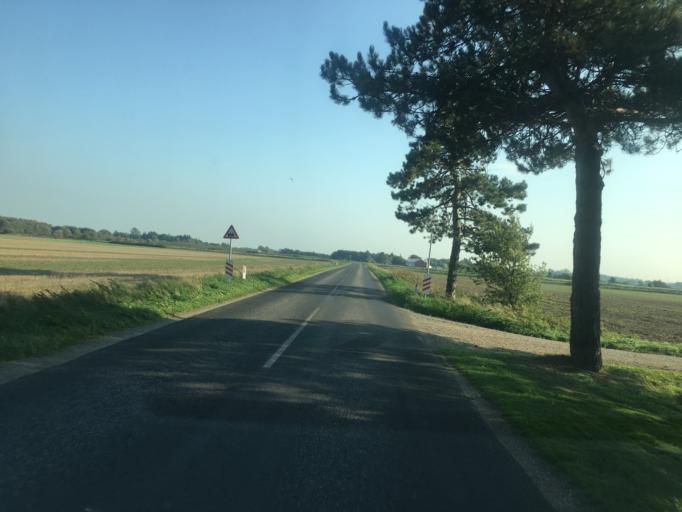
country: DE
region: Schleswig-Holstein
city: Bramstedtlund
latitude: 54.9449
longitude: 9.0623
